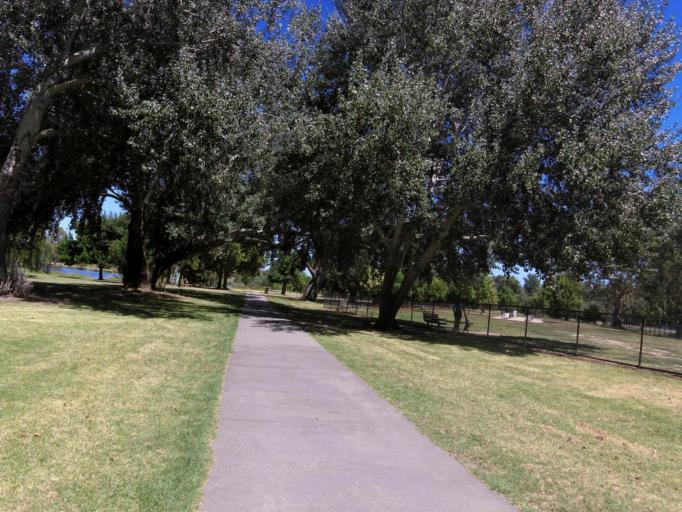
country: AU
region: Victoria
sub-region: Wodonga
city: Wodonga
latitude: -36.1118
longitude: 146.8898
